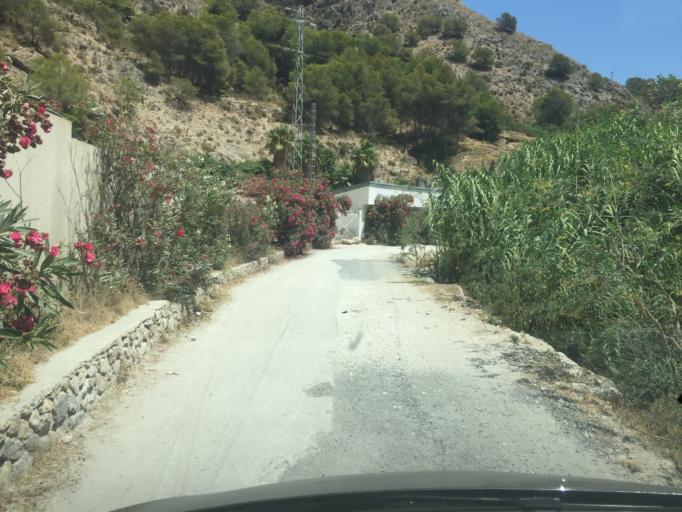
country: ES
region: Andalusia
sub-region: Provincia de Malaga
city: Nerja
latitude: 36.7716
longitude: -3.8790
